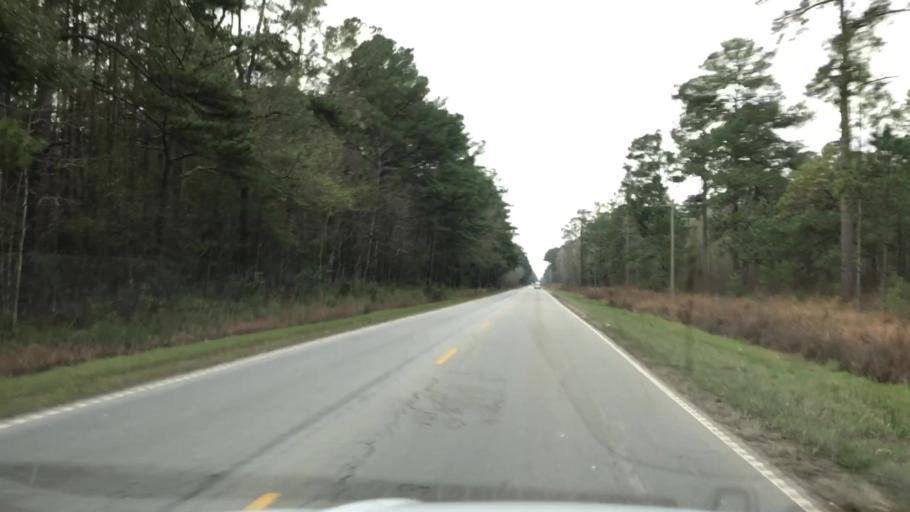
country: US
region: South Carolina
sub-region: Jasper County
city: Ridgeland
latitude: 32.3797
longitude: -80.9112
